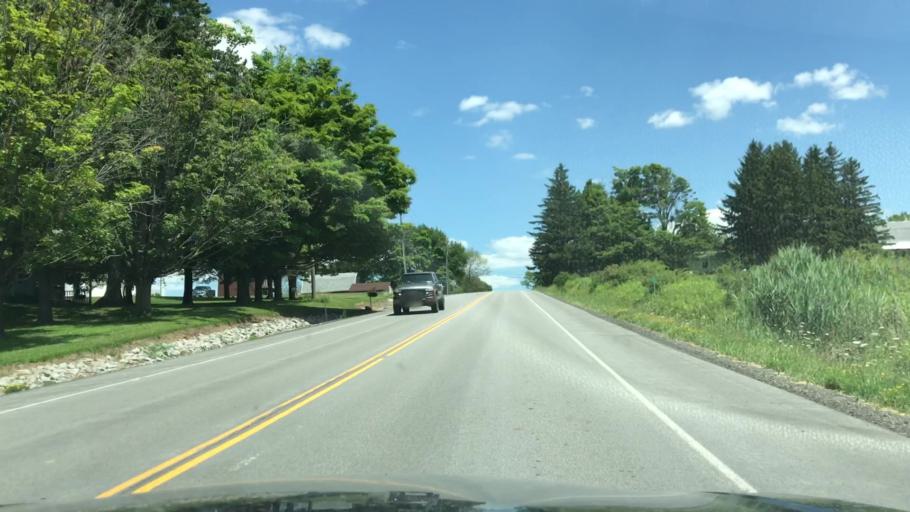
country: US
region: New York
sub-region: Erie County
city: Alden
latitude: 42.7698
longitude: -78.4327
